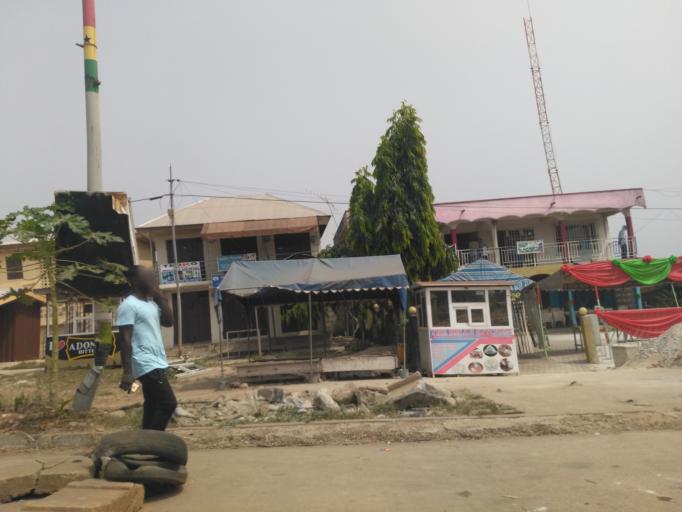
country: GH
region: Ashanti
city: Kumasi
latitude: 6.6934
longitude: -1.6454
